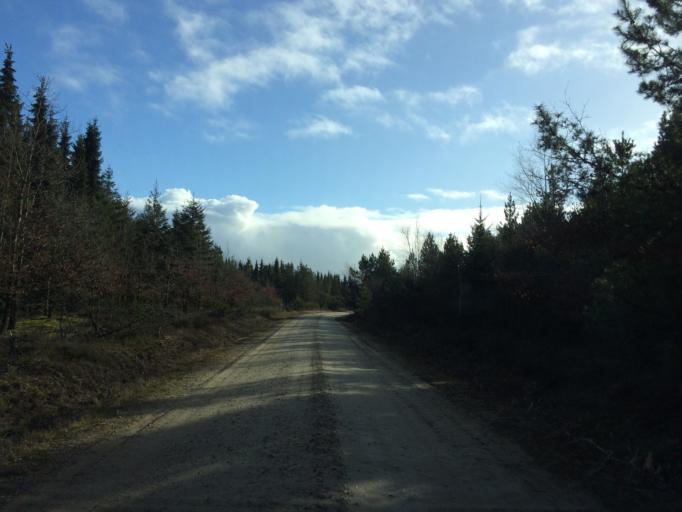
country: DK
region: Central Jutland
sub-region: Holstebro Kommune
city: Ulfborg
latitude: 56.2763
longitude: 8.3728
